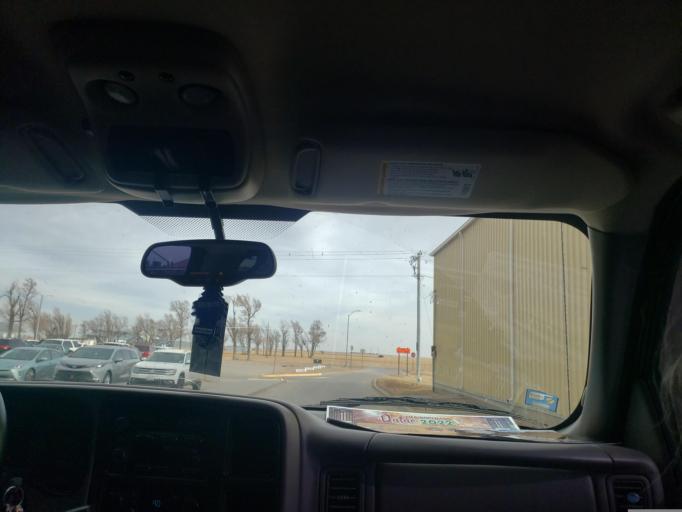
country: US
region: Kansas
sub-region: Finney County
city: Garden City
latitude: 37.9263
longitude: -100.7191
